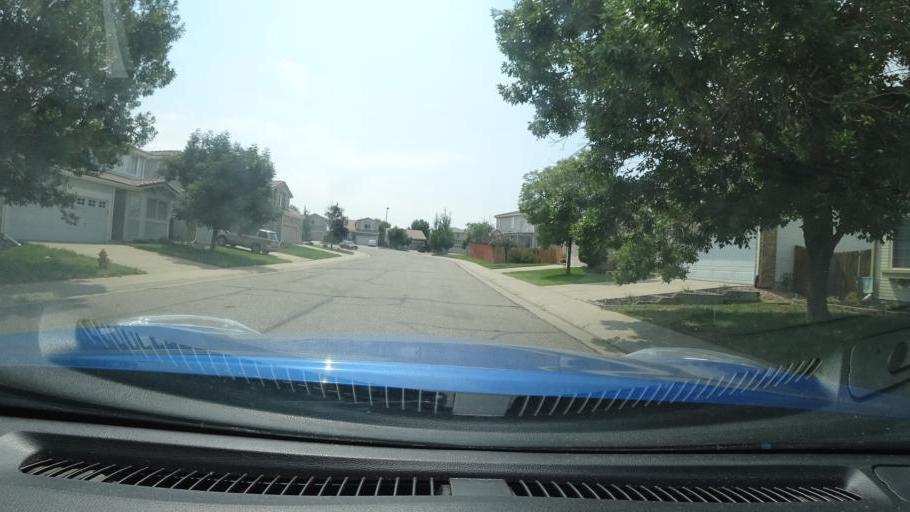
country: US
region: Colorado
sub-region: Adams County
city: Aurora
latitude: 39.7790
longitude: -104.7566
